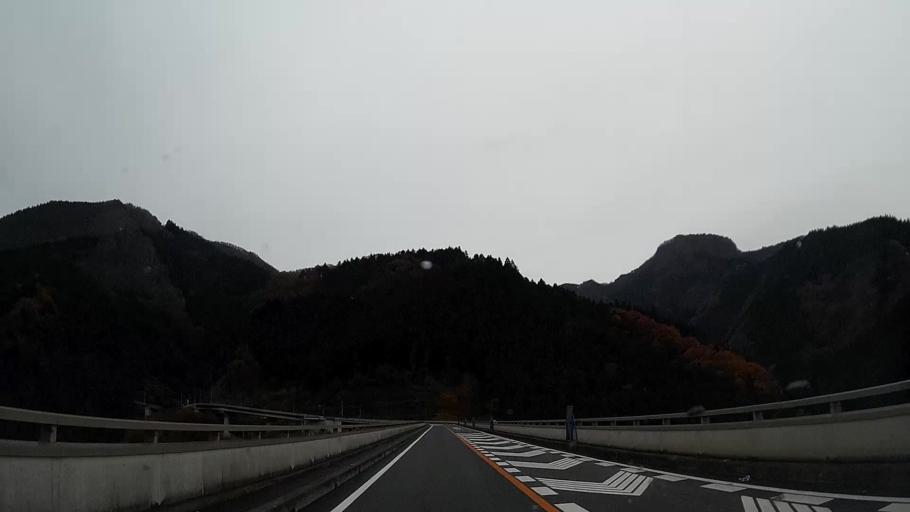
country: JP
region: Saitama
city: Chichibu
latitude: 35.9563
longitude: 138.9045
